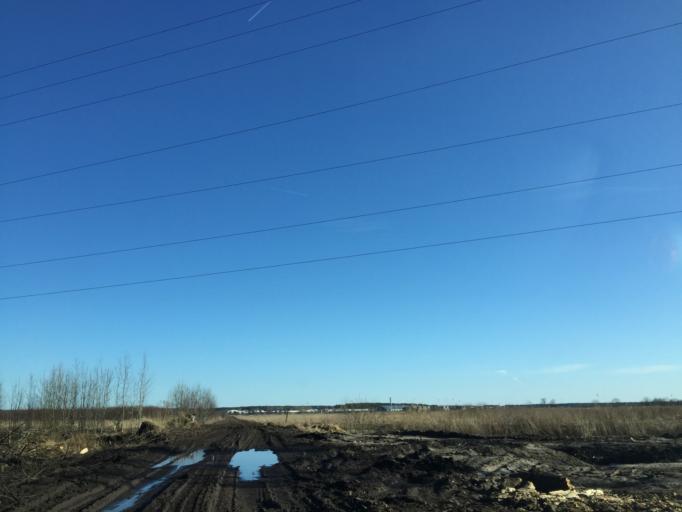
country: LV
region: Babite
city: Pinki
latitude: 56.9668
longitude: 23.8843
